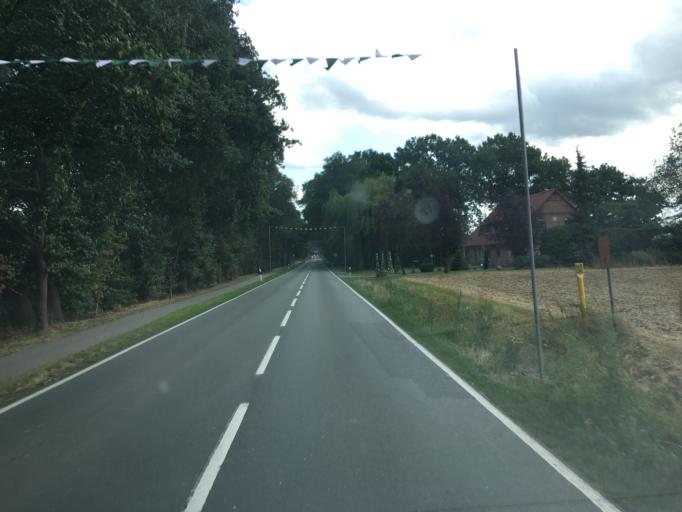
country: DE
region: Lower Saxony
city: Friesoythe
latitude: 53.0760
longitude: 7.8443
